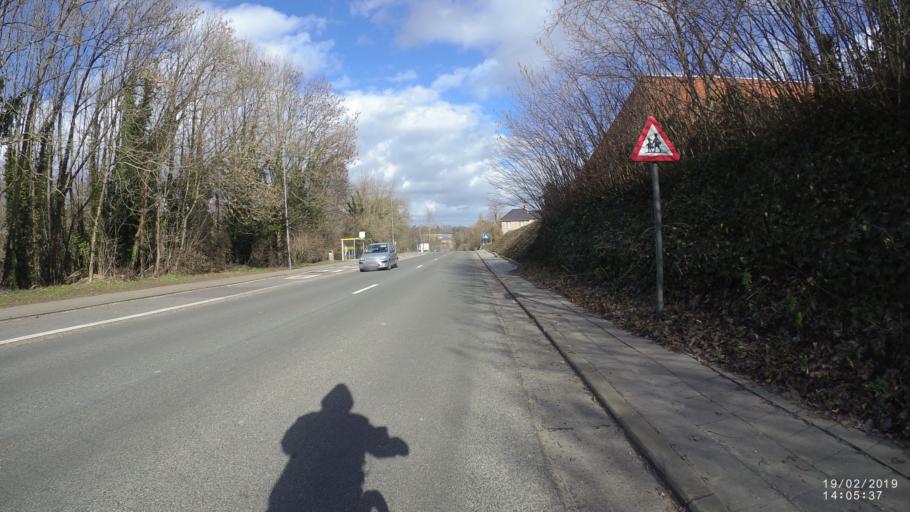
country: BE
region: Flanders
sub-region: Provincie Limburg
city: Tongeren
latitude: 50.7804
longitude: 5.4551
